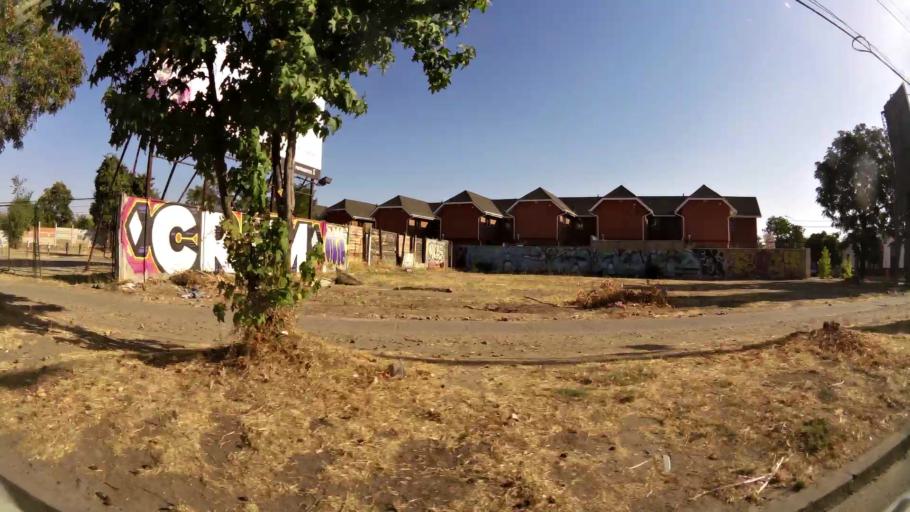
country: CL
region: Maule
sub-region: Provincia de Talca
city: Talca
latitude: -35.4293
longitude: -71.6737
